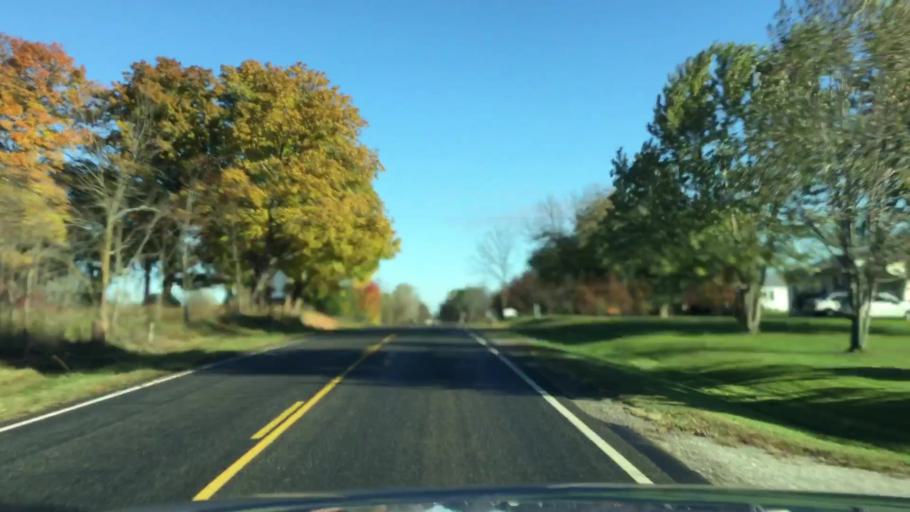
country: US
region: Michigan
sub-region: Shiawassee County
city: Durand
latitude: 42.8464
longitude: -83.9456
